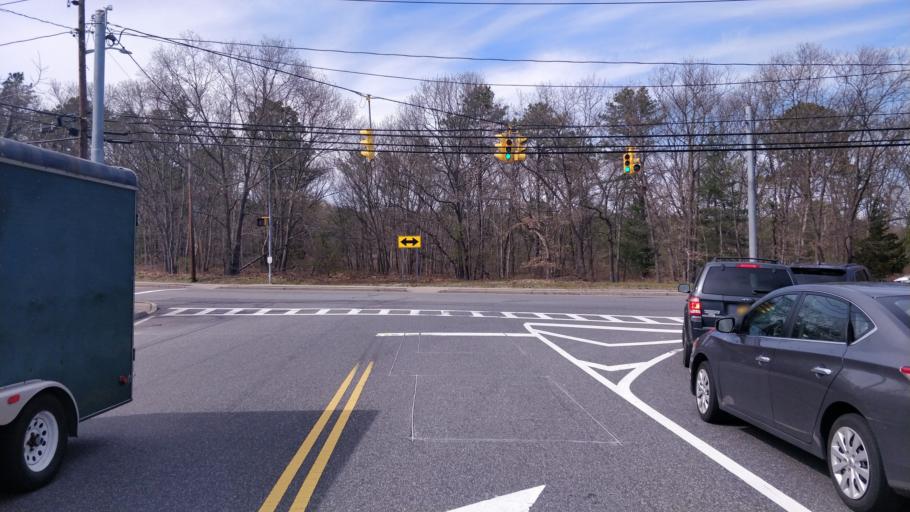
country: US
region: New York
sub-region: Suffolk County
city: Terryville
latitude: 40.8813
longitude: -73.0739
